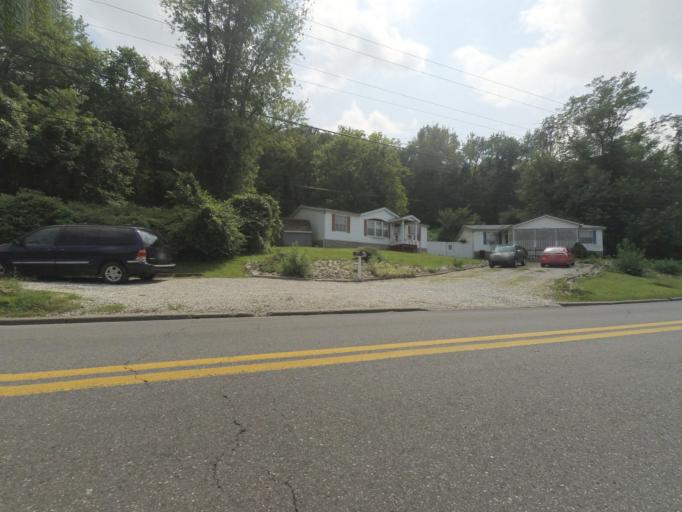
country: US
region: West Virginia
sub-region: Cabell County
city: Huntington
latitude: 38.4220
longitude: -82.4052
